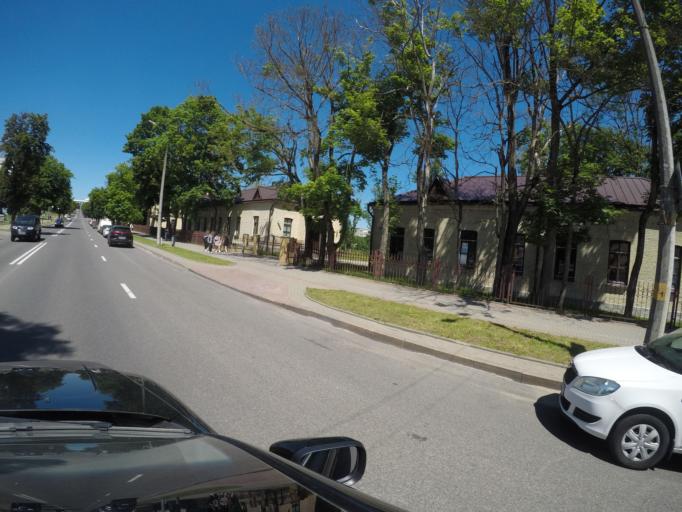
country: BY
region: Grodnenskaya
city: Hrodna
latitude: 53.6854
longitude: 23.8317
